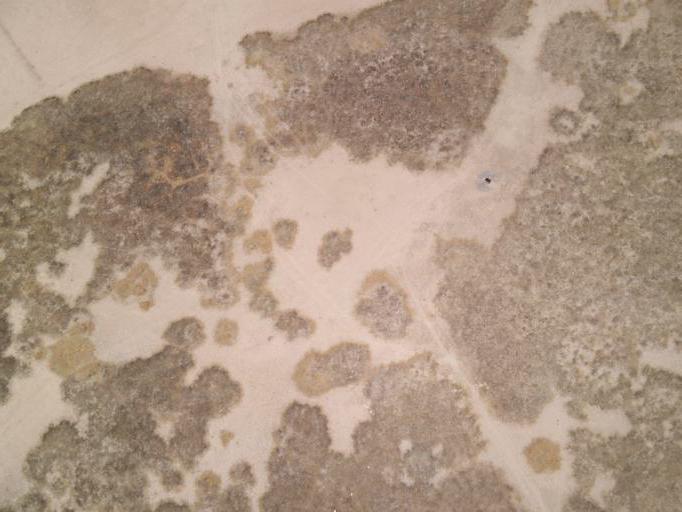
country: BO
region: La Paz
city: Batallas
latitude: -16.3523
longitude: -68.6300
